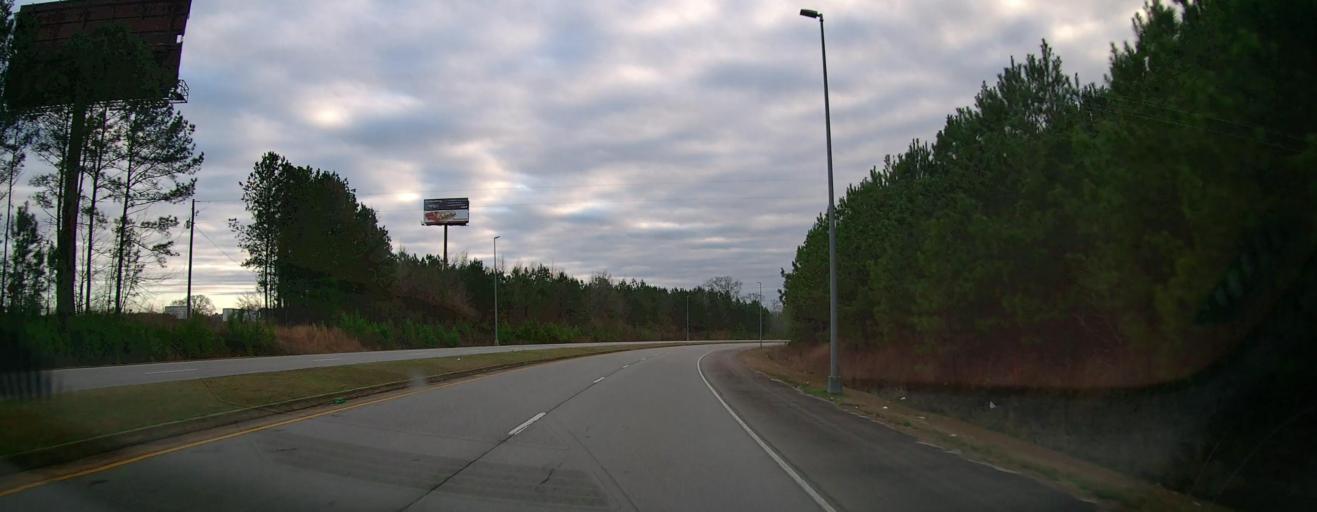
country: US
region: Georgia
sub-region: Troup County
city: West Point
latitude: 32.8859
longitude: -85.1439
